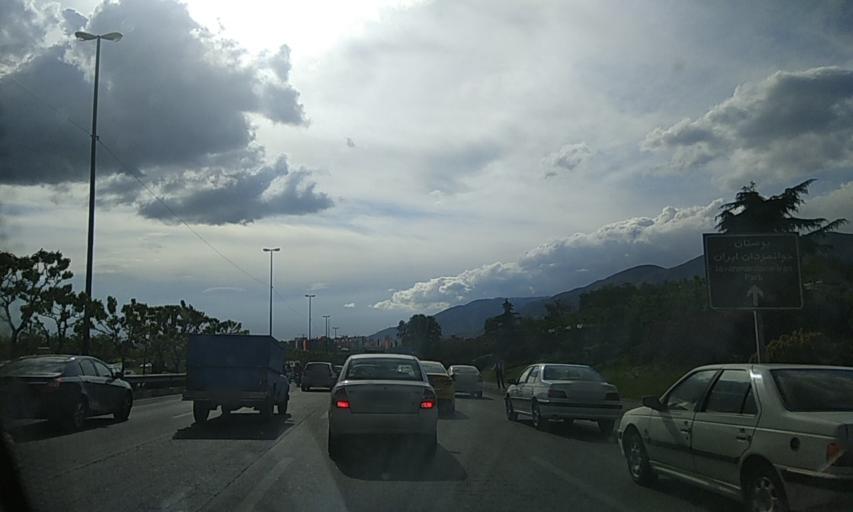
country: IR
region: Tehran
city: Tehran
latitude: 35.7539
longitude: 51.2828
